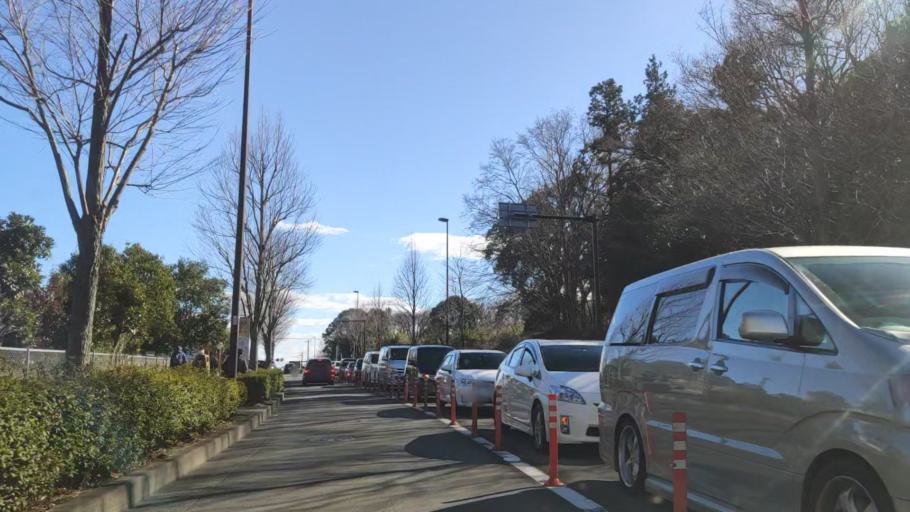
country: JP
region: Tokyo
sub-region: Machida-shi
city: Machida
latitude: 35.5181
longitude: 139.4970
